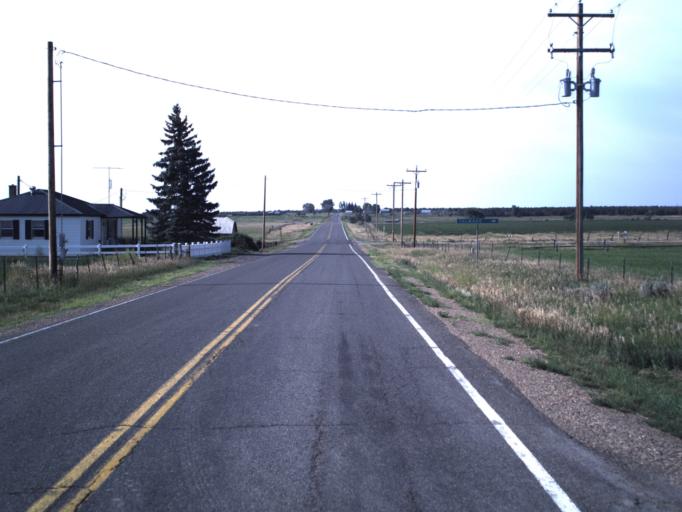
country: US
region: Utah
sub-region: Duchesne County
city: Duchesne
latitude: 40.3412
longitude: -110.4079
